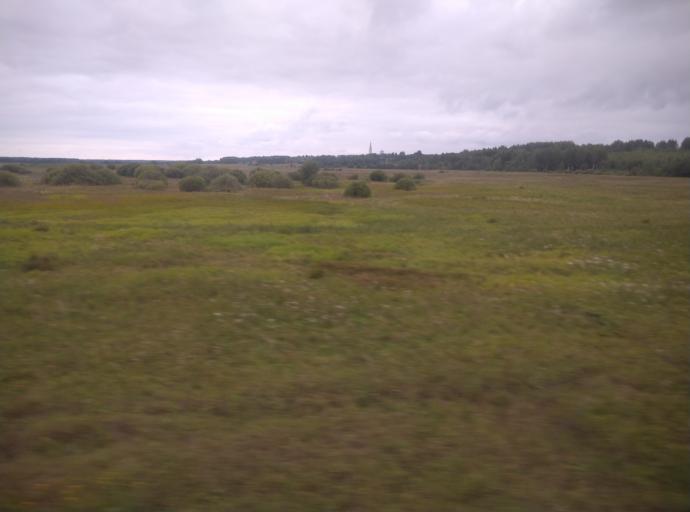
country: RU
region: Kostroma
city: Nerekhta
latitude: 57.4879
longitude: 40.6020
